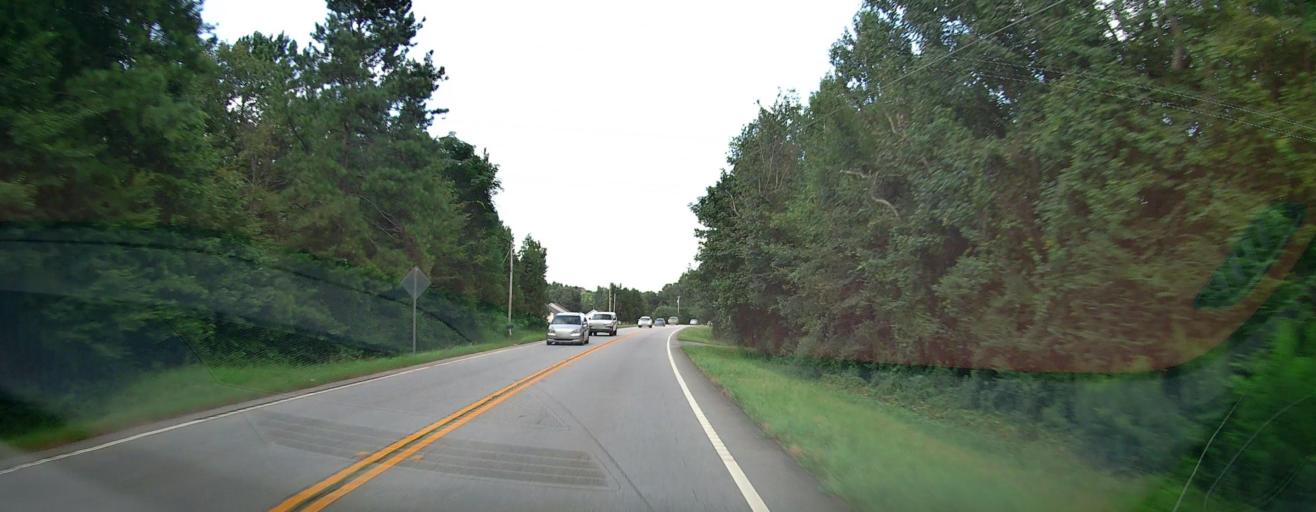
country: US
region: Georgia
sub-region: Coweta County
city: Senoia
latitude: 33.2462
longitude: -84.5649
